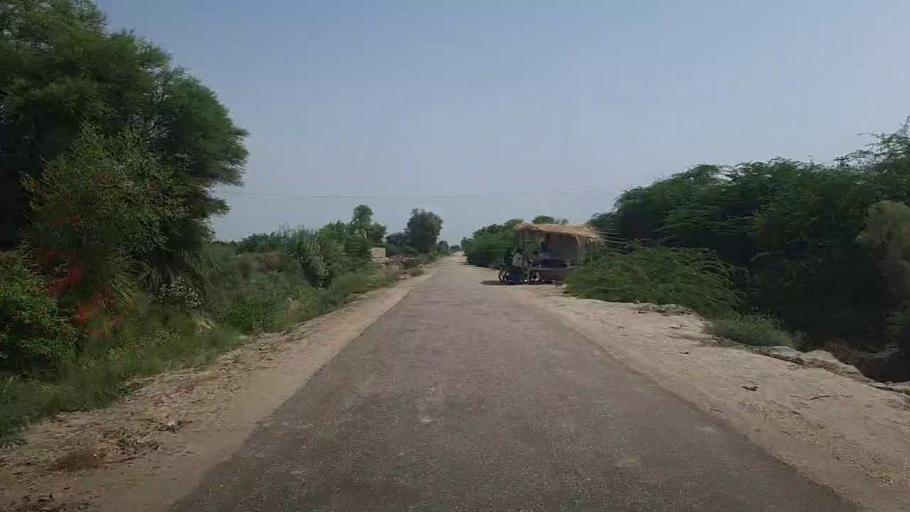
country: PK
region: Sindh
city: Pad Idan
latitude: 26.8203
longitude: 68.3278
